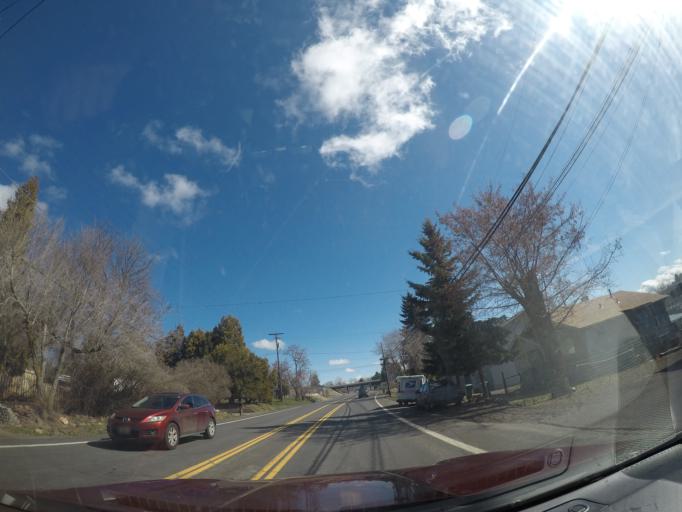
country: US
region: Oregon
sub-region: Klamath County
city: Klamath Falls
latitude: 42.2397
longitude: -121.7995
